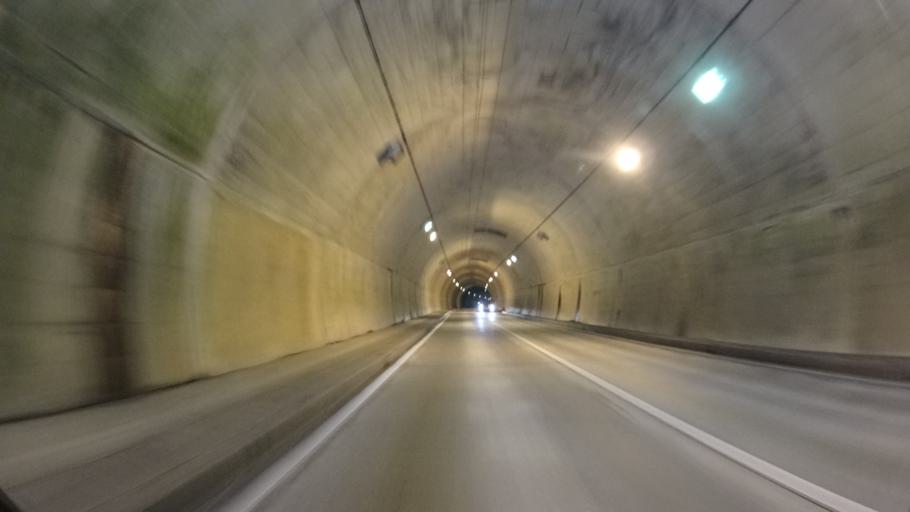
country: JP
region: Ehime
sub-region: Nishiuwa-gun
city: Ikata-cho
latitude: 33.4369
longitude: 132.2349
